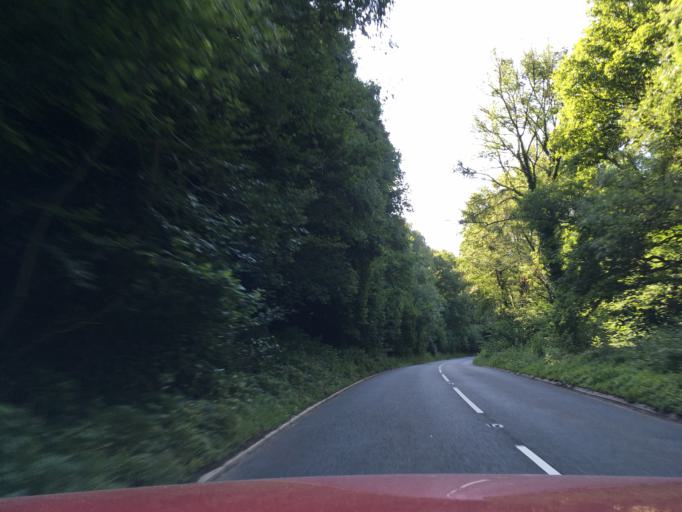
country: GB
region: England
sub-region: Gloucestershire
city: Lydney
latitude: 51.7397
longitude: -2.5395
